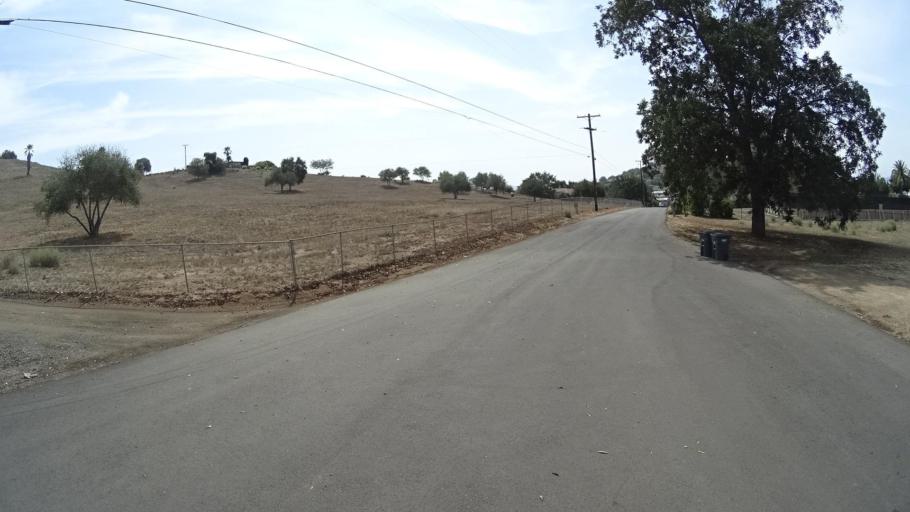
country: US
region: California
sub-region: San Diego County
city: Escondido
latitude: 33.1072
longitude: -117.0350
